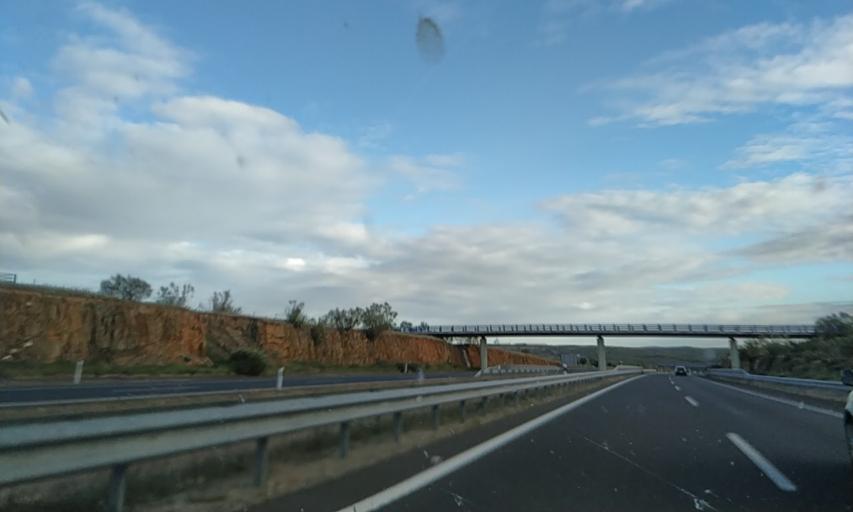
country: ES
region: Extremadura
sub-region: Provincia de Caceres
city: Hinojal
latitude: 39.6865
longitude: -6.3984
